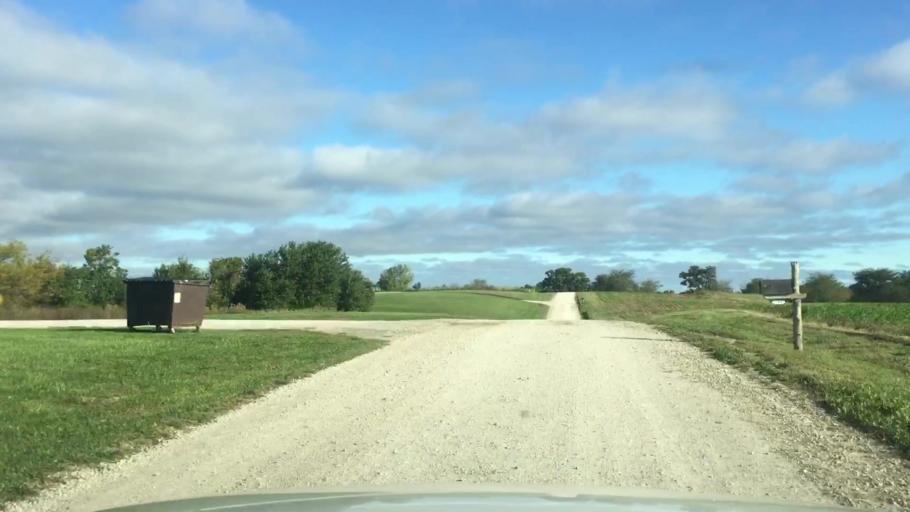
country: US
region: Missouri
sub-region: Howard County
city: New Franklin
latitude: 39.0798
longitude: -92.7516
